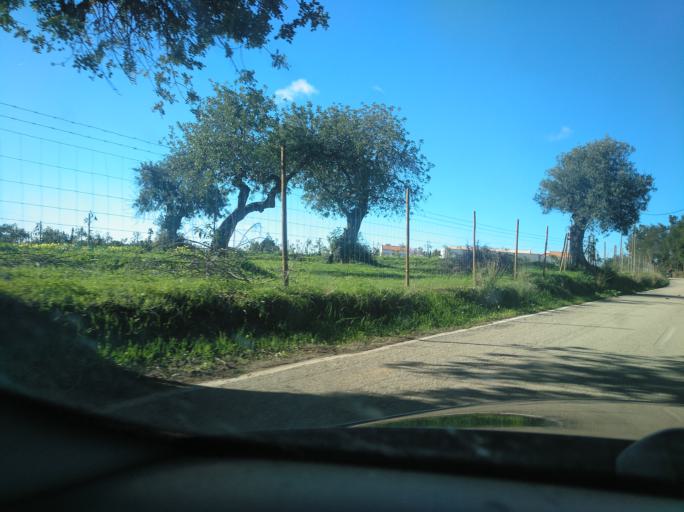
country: PT
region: Faro
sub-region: Tavira
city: Tavira
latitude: 37.1589
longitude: -7.5555
